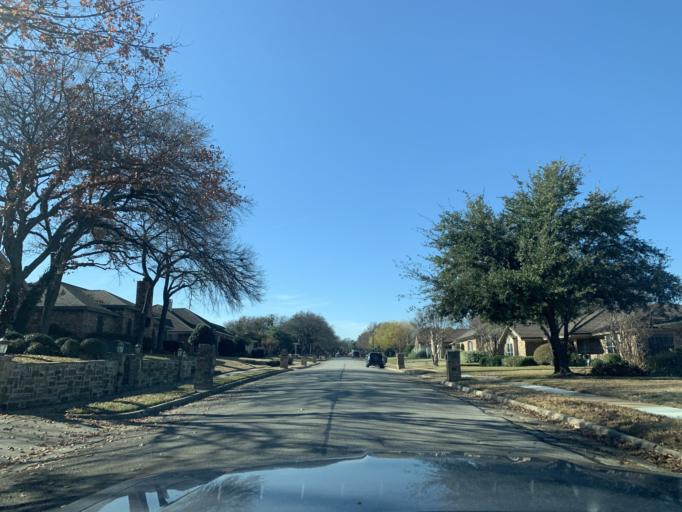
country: US
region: Texas
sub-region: Tarrant County
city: Bedford
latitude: 32.8434
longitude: -97.1551
